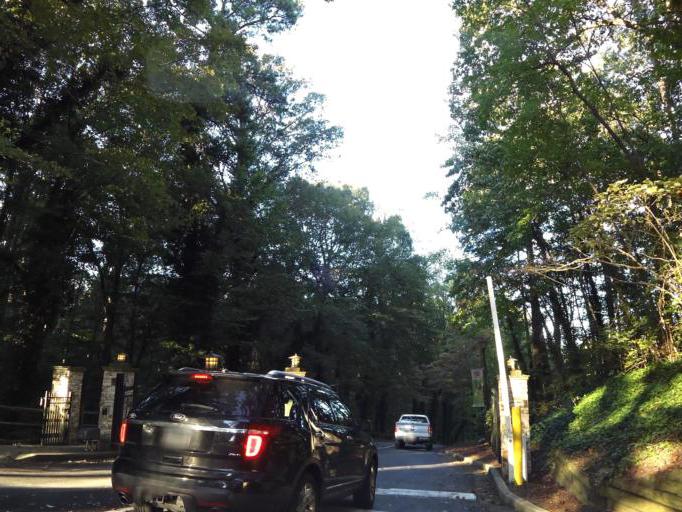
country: US
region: Georgia
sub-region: Cobb County
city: Vinings
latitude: 33.9036
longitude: -84.4533
